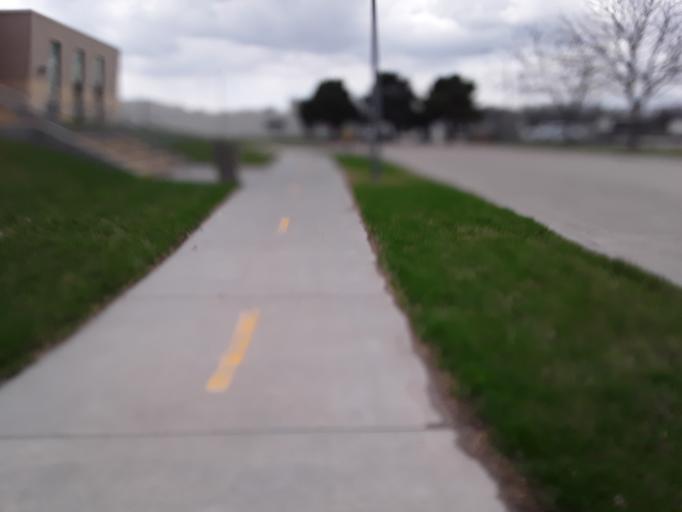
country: US
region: Nebraska
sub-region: Lancaster County
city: Lincoln
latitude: 40.8341
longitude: -96.6831
